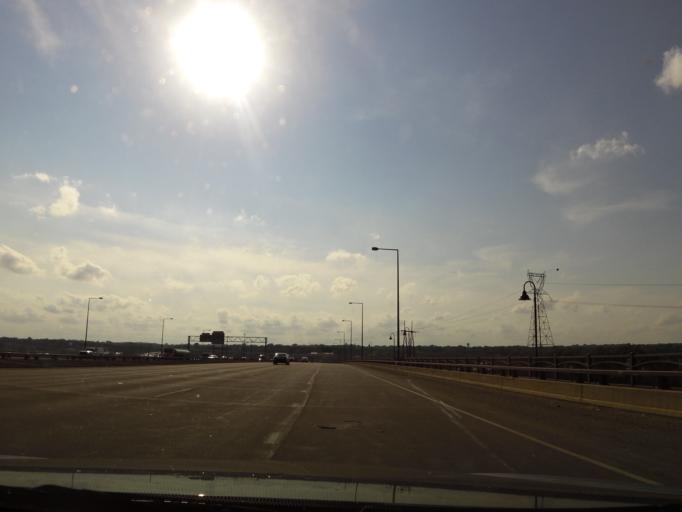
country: US
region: Minnesota
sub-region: Dakota County
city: South Saint Paul
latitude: 44.8834
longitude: -93.0151
